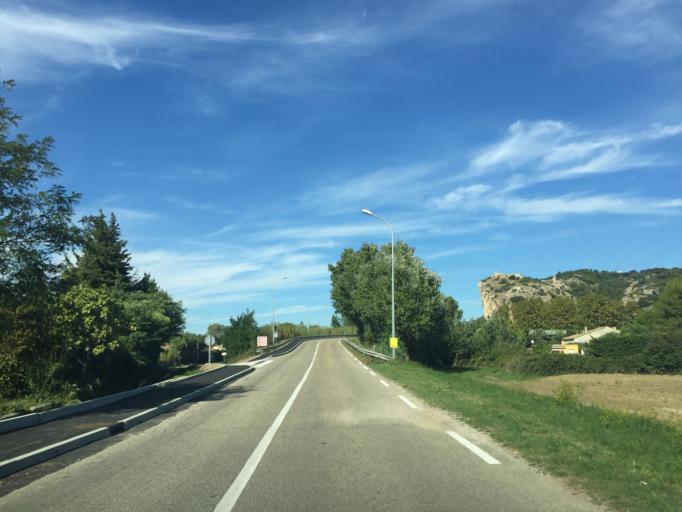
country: FR
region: Provence-Alpes-Cote d'Azur
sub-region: Departement du Vaucluse
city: Mornas
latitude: 44.1972
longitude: 4.7275
